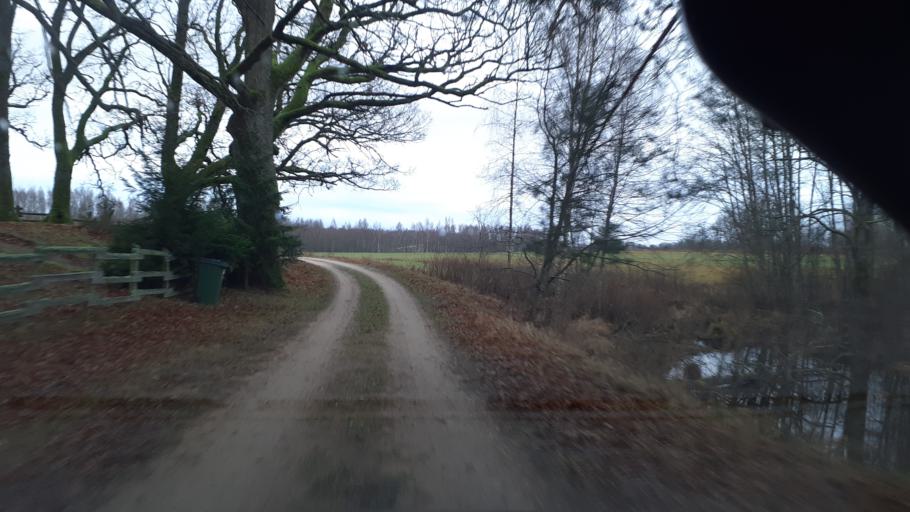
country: LV
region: Kuldigas Rajons
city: Kuldiga
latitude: 56.8785
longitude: 21.7704
